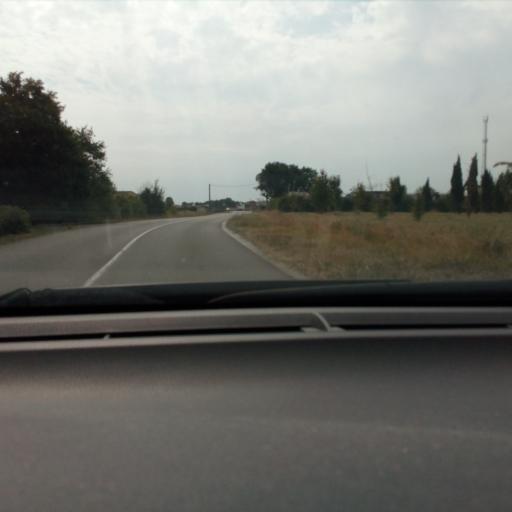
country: FR
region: Poitou-Charentes
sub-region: Departement de la Charente
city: Saint-Yrieix-sur-Charente
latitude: 45.6847
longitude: 0.1047
